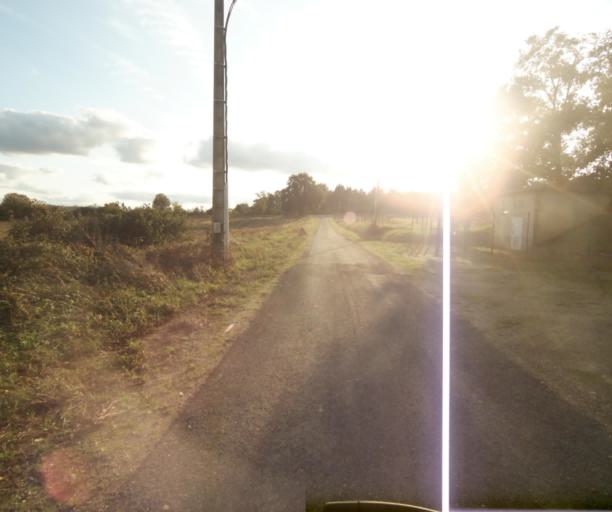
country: FR
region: Midi-Pyrenees
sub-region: Departement de la Haute-Garonne
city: Launac
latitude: 43.8231
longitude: 1.1251
